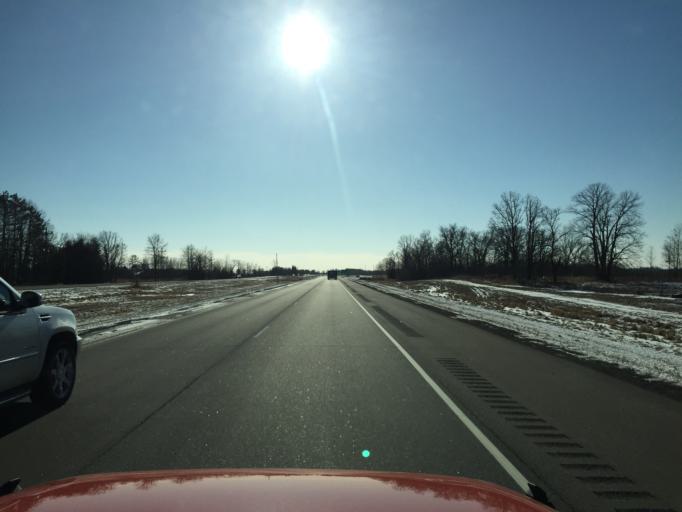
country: US
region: Minnesota
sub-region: Mille Lacs County
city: Milaca
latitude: 45.8016
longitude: -93.6549
